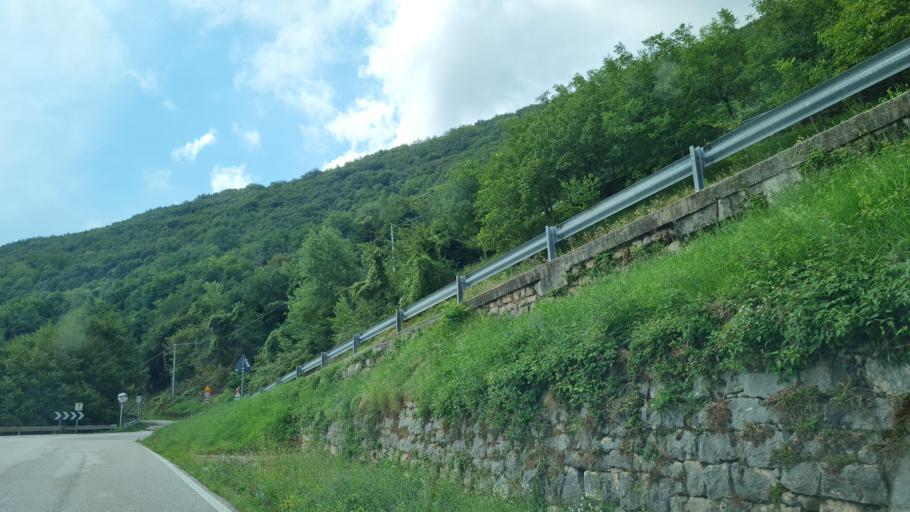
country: IT
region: Veneto
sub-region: Provincia di Vicenza
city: Conco
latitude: 45.7901
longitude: 11.6508
